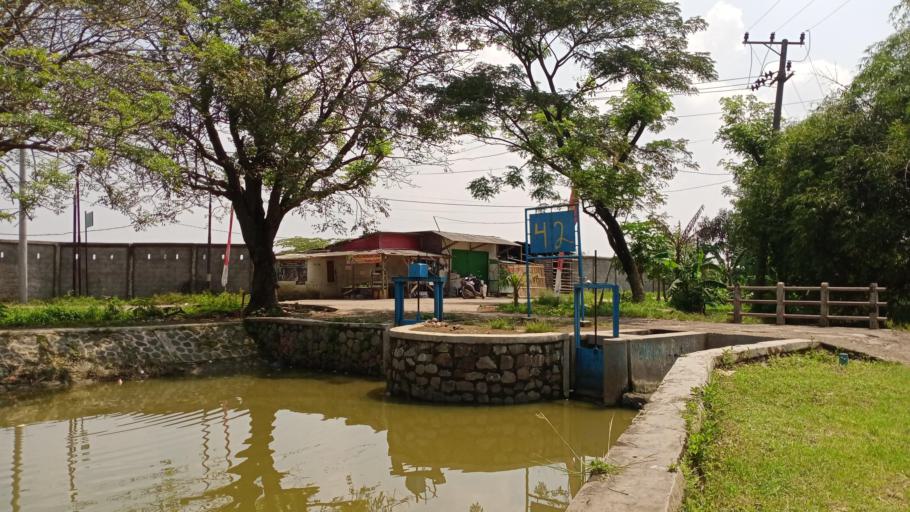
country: ID
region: West Java
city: Cileungsir
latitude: -6.4059
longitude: 107.1004
